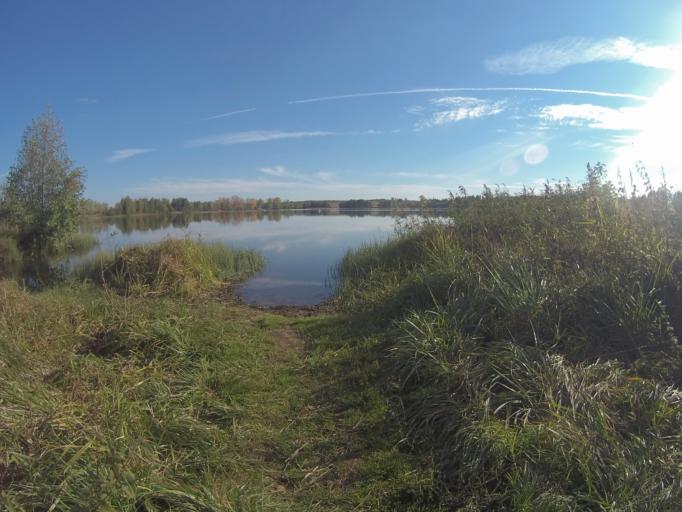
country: RU
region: Vladimir
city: Golovino
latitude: 55.9751
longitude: 40.4511
